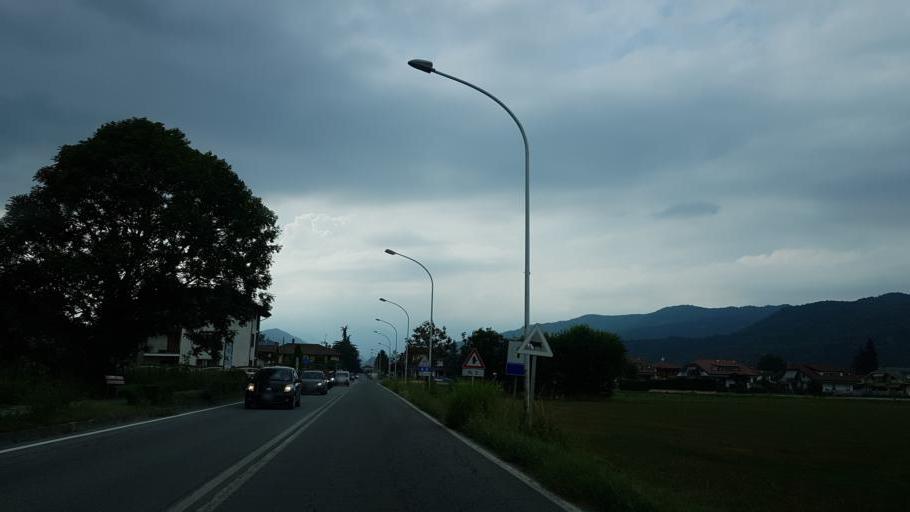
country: IT
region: Piedmont
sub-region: Provincia di Cuneo
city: Borgo San Dalmazzo
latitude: 44.3319
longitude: 7.4766
